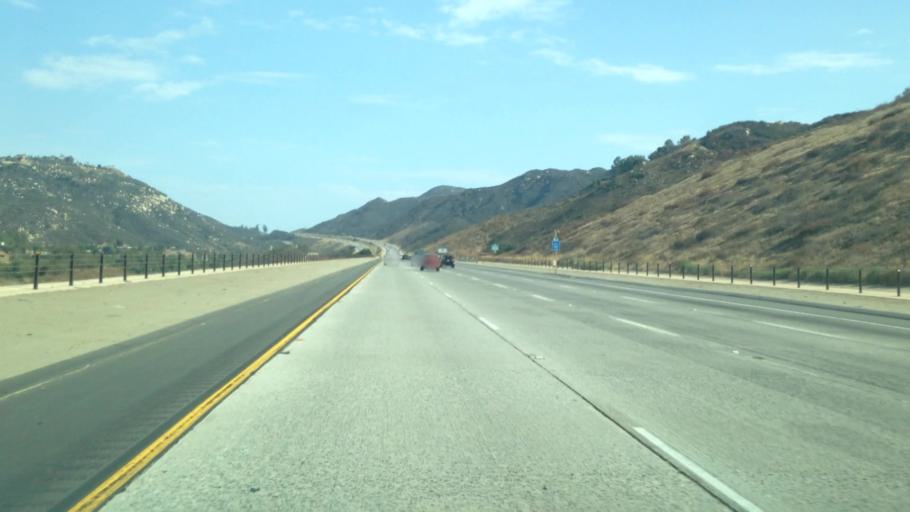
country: US
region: California
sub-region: San Diego County
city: Hidden Meadows
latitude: 33.2380
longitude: -117.1496
